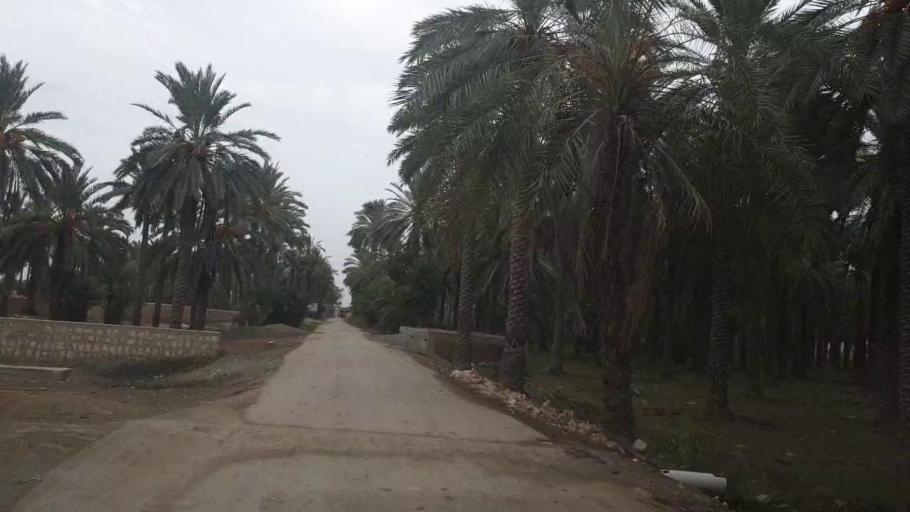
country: PK
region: Sindh
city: Khairpur
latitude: 27.5531
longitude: 68.7507
